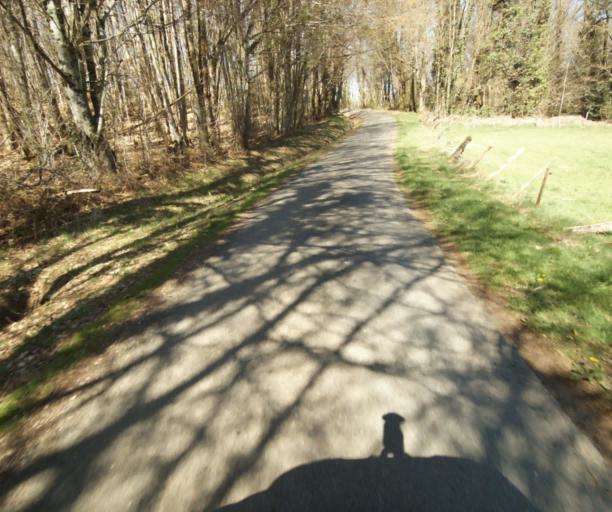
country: FR
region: Limousin
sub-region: Departement de la Correze
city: Saint-Clement
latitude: 45.3871
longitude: 1.6523
